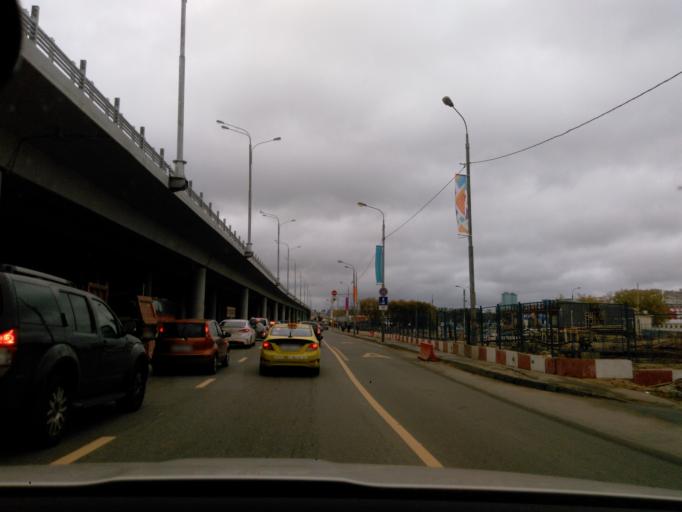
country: RU
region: Moscow
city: Strogino
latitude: 55.8250
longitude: 37.4313
